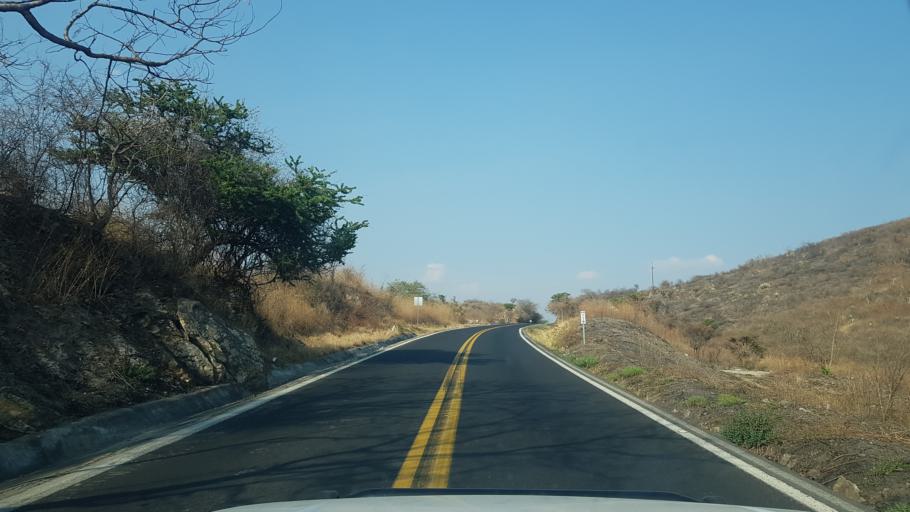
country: MX
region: Puebla
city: Calmeca
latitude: 18.6430
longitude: -98.6065
